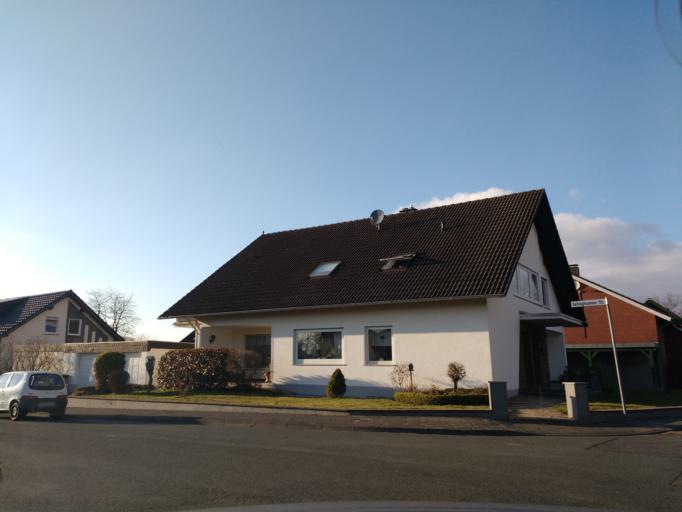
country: DE
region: North Rhine-Westphalia
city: Bad Lippspringe
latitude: 51.7494
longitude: 8.8496
